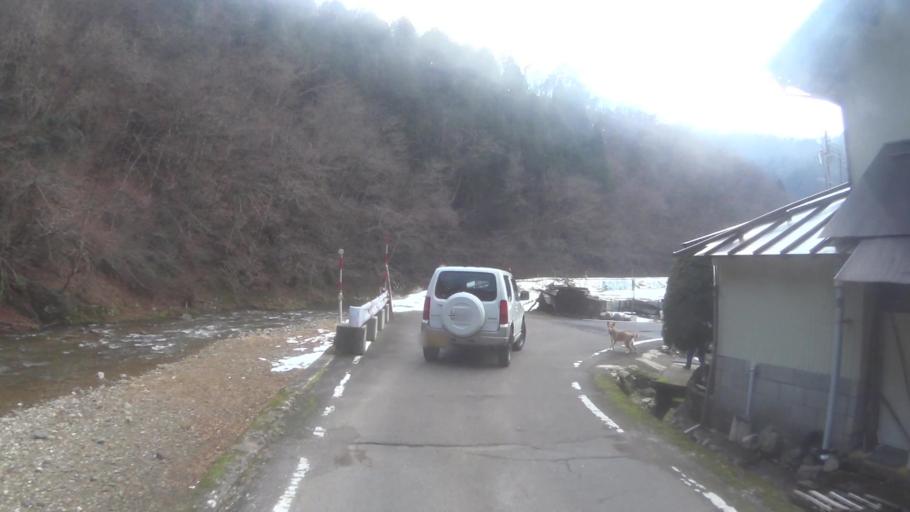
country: JP
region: Kyoto
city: Maizuru
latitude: 35.3978
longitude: 135.4858
